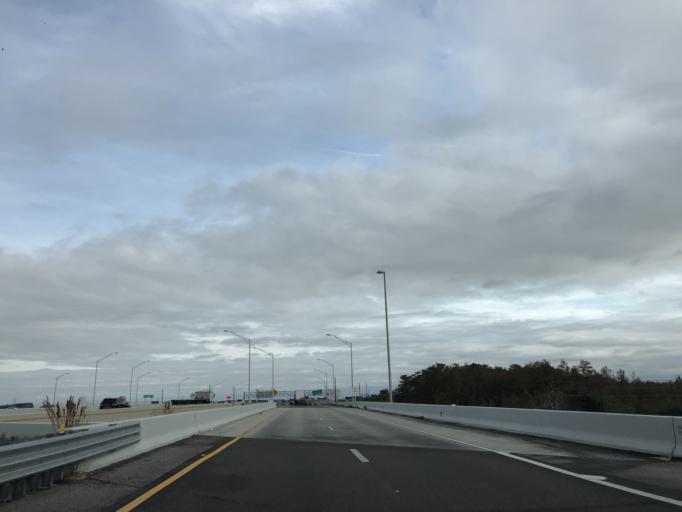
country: US
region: Florida
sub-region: Orange County
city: Meadow Woods
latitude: 28.3678
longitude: -81.3828
